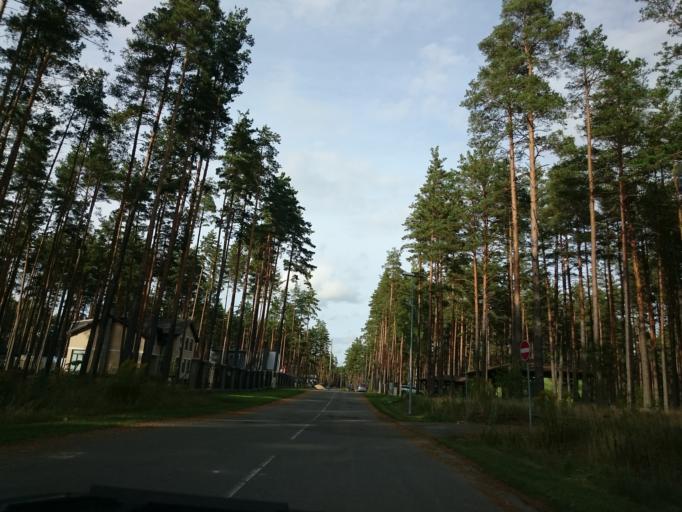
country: LV
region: Adazi
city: Adazi
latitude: 57.0531
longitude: 24.3601
